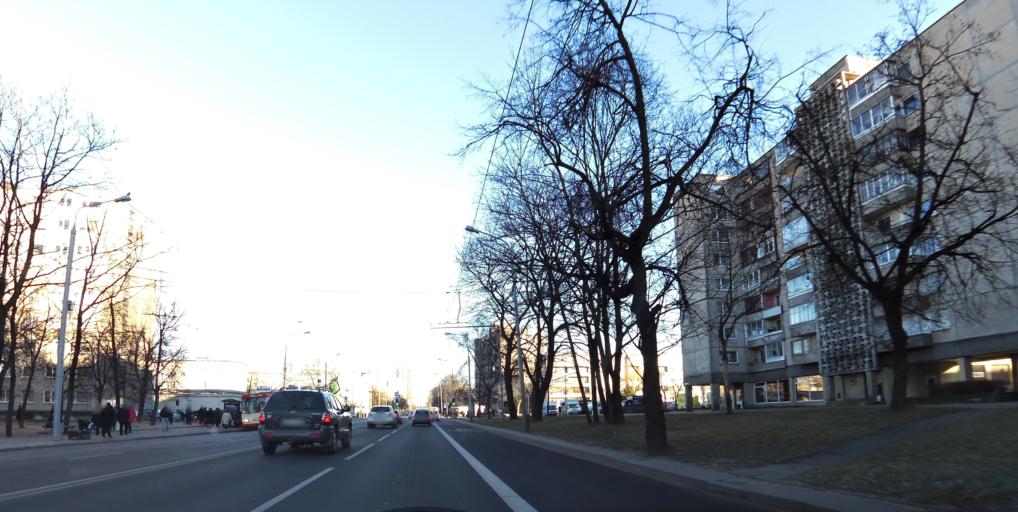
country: LT
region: Vilnius County
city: Vilkpede
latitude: 54.6731
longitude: 25.2467
